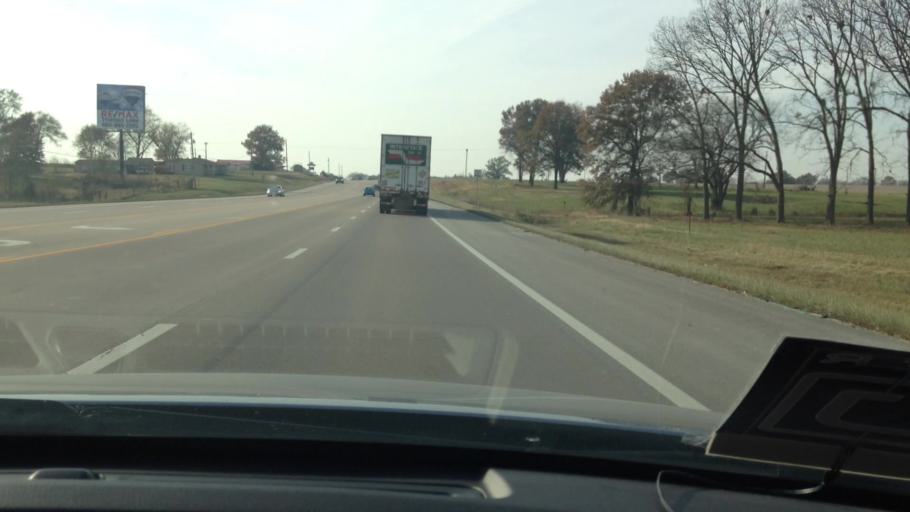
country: US
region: Missouri
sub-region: Henry County
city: Clinton
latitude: 38.3897
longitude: -93.8123
